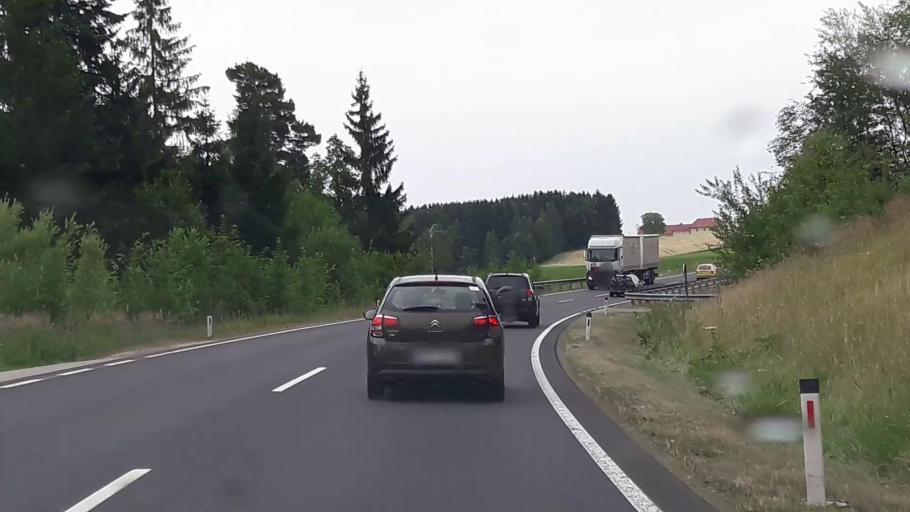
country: AT
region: Upper Austria
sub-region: Politischer Bezirk Rohrbach
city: Kleinzell im Muehlkreis
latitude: 48.4433
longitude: 14.0432
